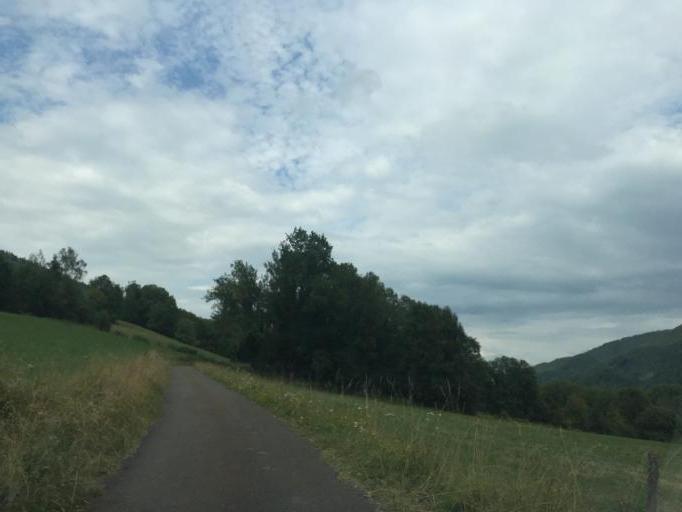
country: FR
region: Franche-Comte
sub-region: Departement du Jura
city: Longchaumois
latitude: 46.4702
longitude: 5.8986
